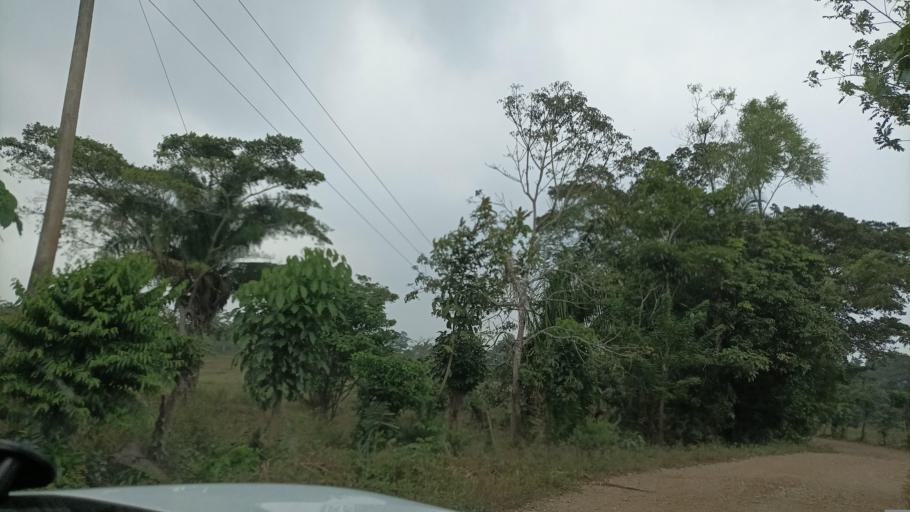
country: MX
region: Veracruz
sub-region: Uxpanapa
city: Poblado 10
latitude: 17.5694
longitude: -94.2273
